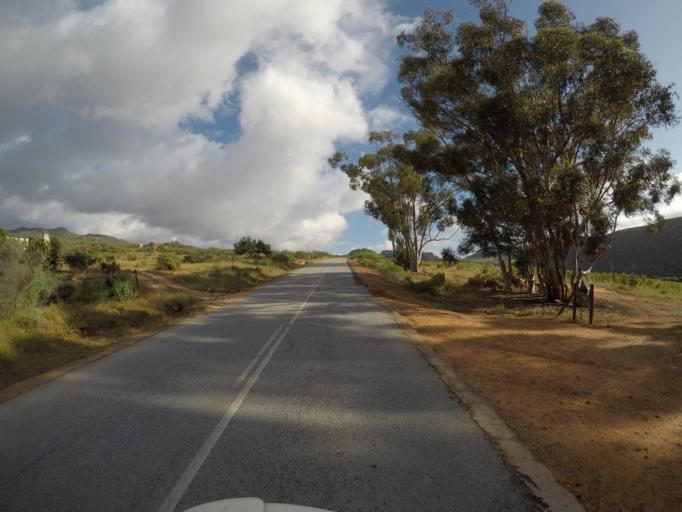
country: ZA
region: Western Cape
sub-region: West Coast District Municipality
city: Clanwilliam
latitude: -32.4320
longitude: 18.9392
